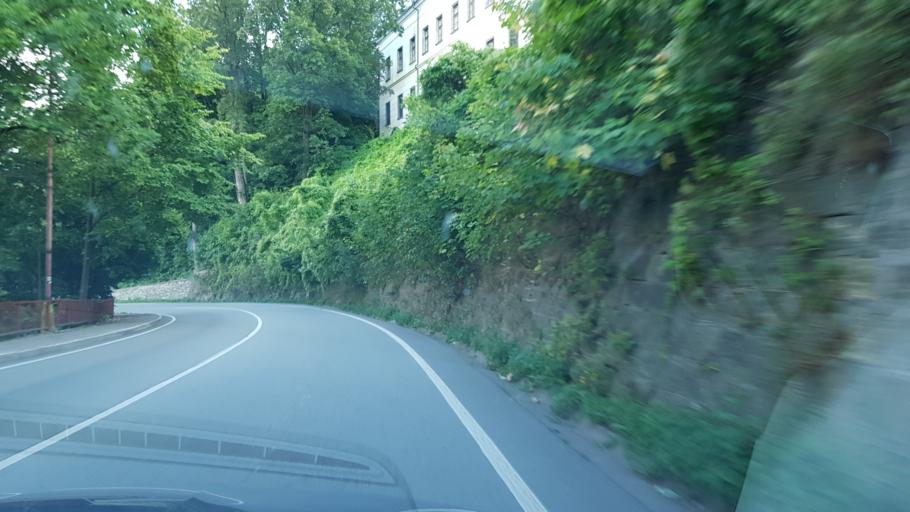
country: CZ
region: Pardubicky
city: Zamberk
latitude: 50.0863
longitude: 16.4676
